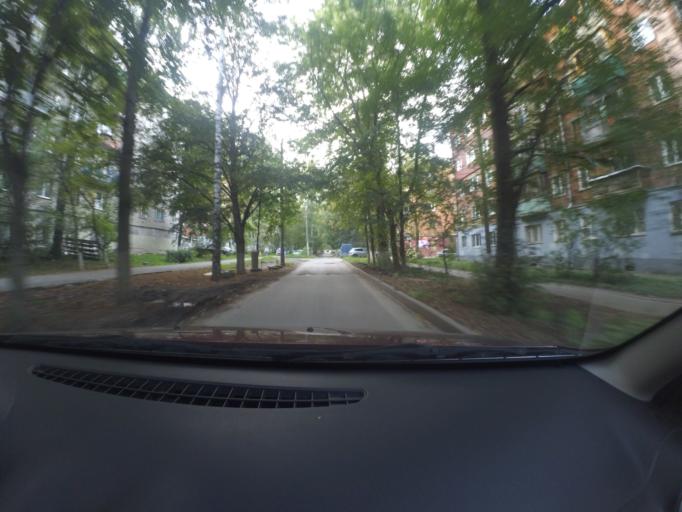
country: RU
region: Nizjnij Novgorod
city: Nizhniy Novgorod
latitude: 56.2797
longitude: 43.9869
